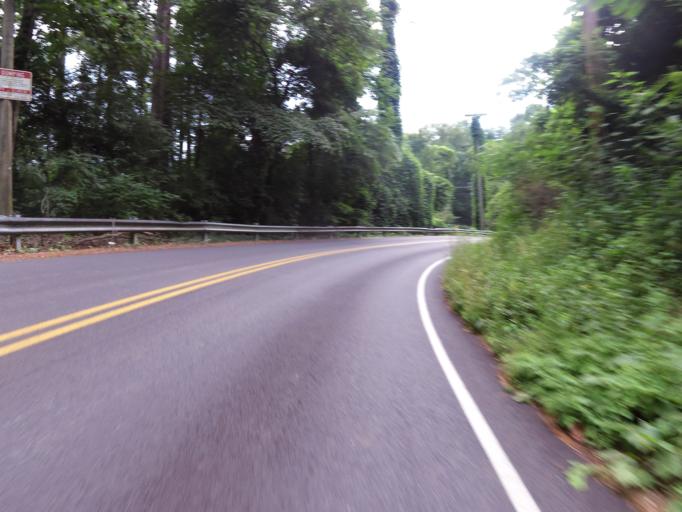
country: US
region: Tennessee
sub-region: Knox County
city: Knoxville
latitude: 35.9712
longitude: -83.8724
